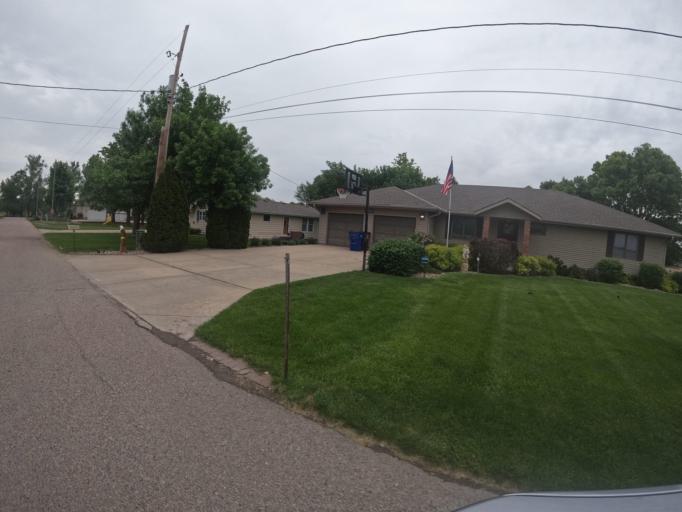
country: US
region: Nebraska
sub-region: Sarpy County
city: Offutt Air Force Base
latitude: 41.0550
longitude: -95.9556
